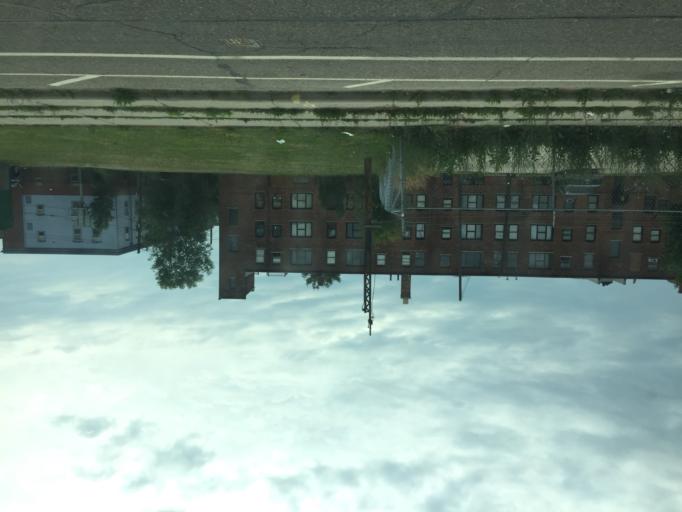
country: US
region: Michigan
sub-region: Wayne County
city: Detroit
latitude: 42.3463
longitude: -83.0664
